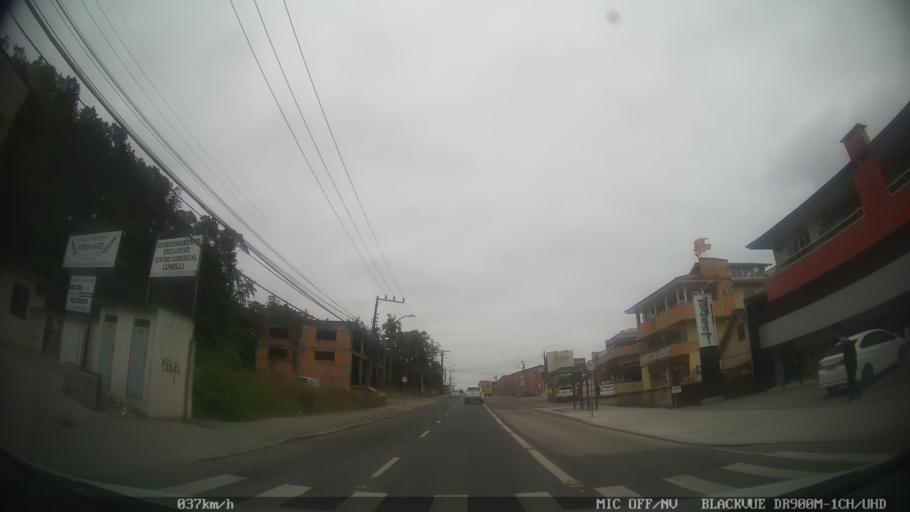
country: BR
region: Santa Catarina
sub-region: Joinville
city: Joinville
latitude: -26.3421
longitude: -48.8473
